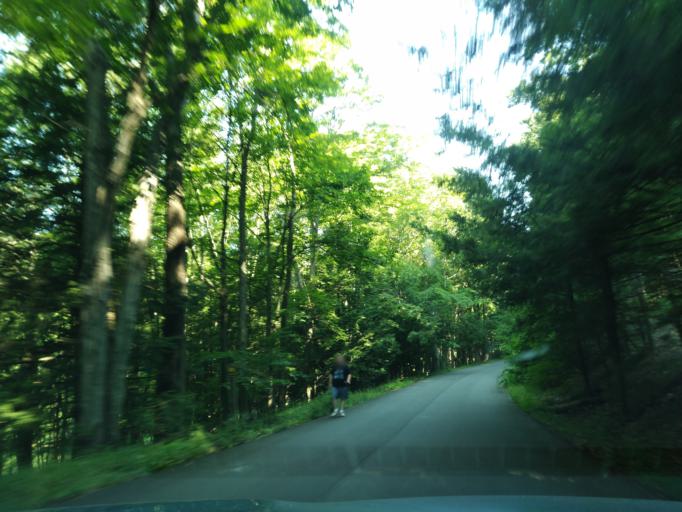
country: US
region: Connecticut
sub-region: New Haven County
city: Southbury
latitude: 41.4244
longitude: -73.2056
